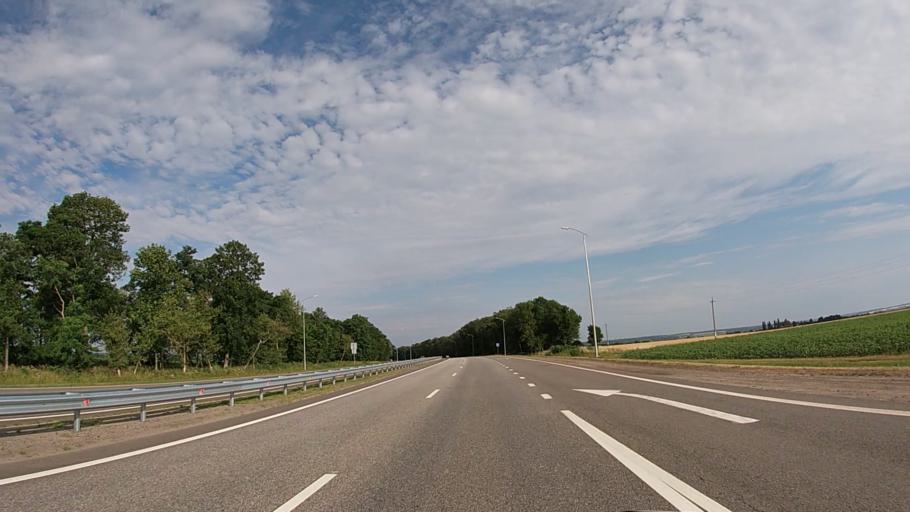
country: RU
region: Belgorod
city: Tomarovka
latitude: 50.6818
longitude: 36.2870
